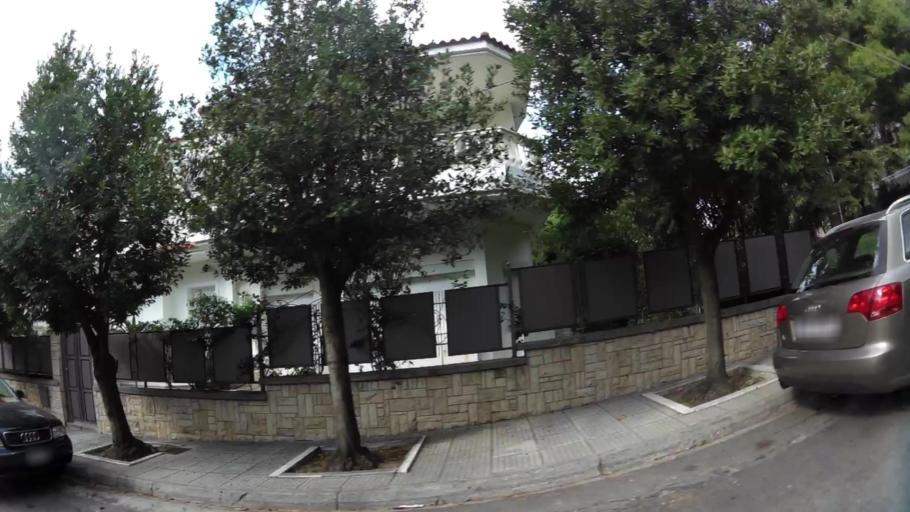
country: GR
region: Attica
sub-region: Nomarchia Athinas
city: Melissia
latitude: 38.0572
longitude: 23.8310
